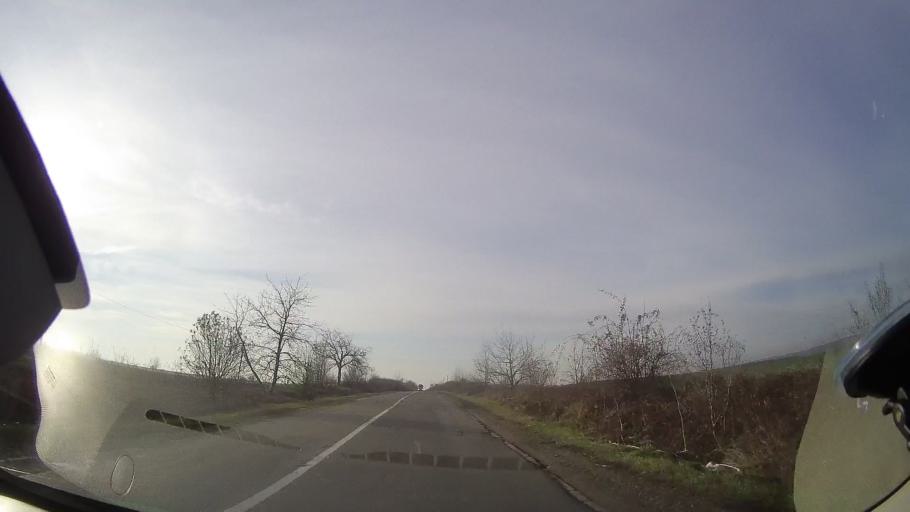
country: RO
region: Bihor
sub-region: Comuna Ciuhoiu
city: Ciuhoiu
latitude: 47.2257
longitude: 22.1395
